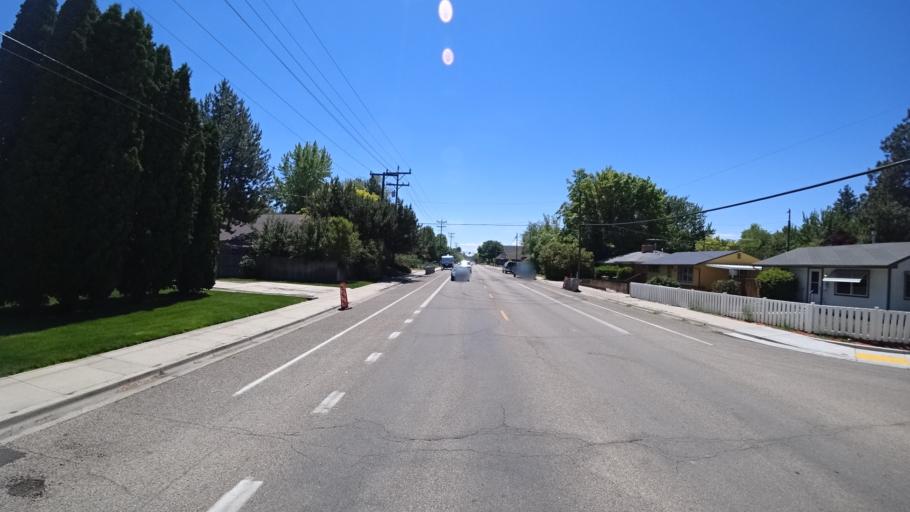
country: US
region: Idaho
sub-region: Ada County
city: Garden City
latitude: 43.5989
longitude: -116.2286
